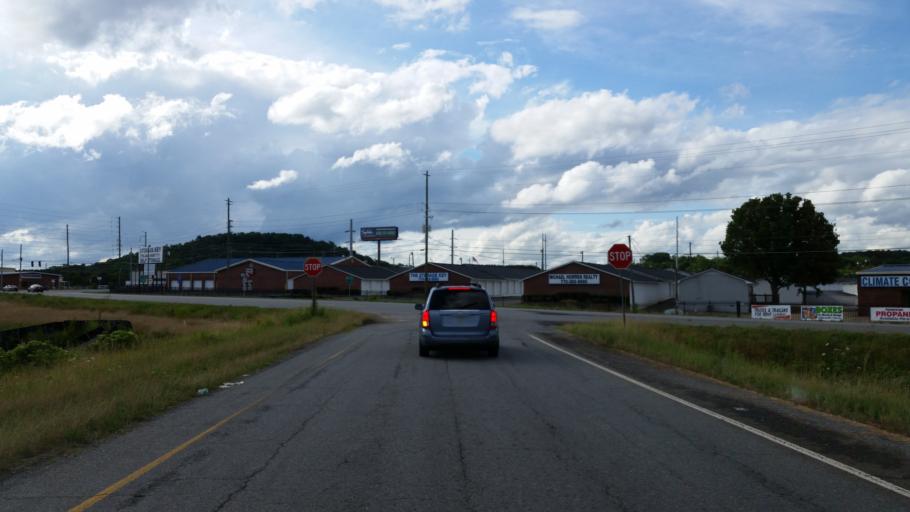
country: US
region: Georgia
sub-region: Bartow County
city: Cartersville
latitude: 34.2017
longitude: -84.7978
